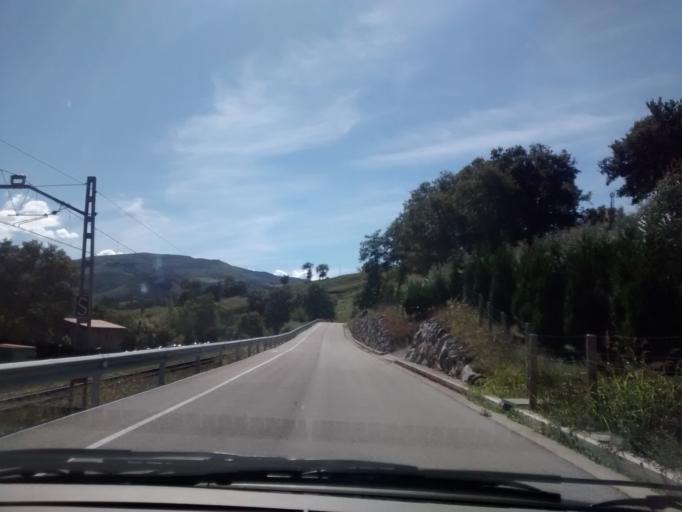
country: ES
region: Cantabria
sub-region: Provincia de Cantabria
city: Lierganes
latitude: 43.3570
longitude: -3.7130
